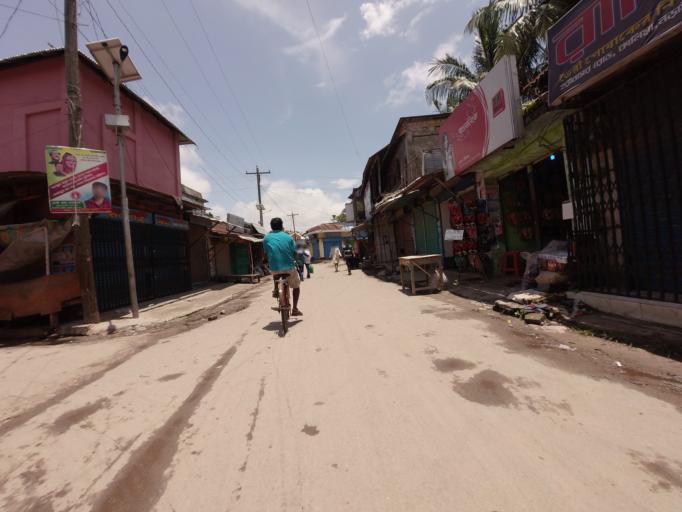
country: BD
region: Khulna
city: Kalia
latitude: 23.0425
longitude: 89.6306
